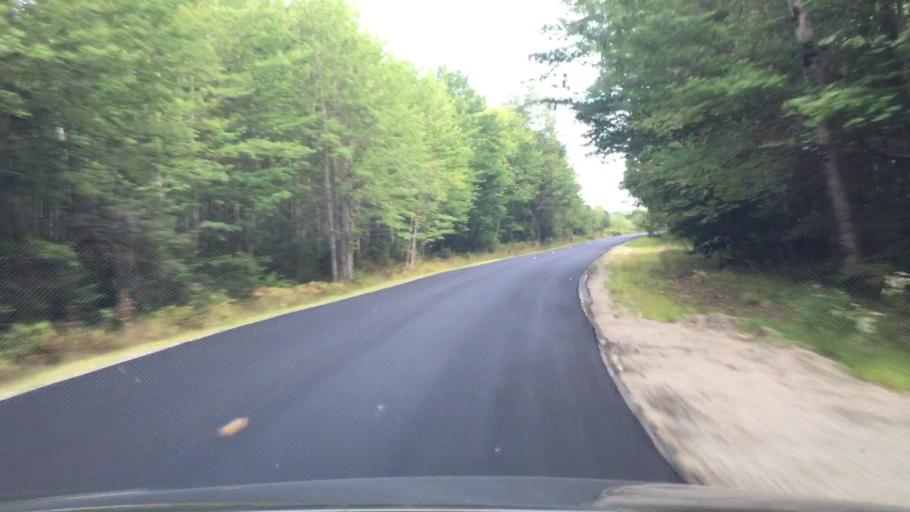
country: US
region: Maine
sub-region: Hancock County
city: Orland
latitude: 44.5432
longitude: -68.6172
